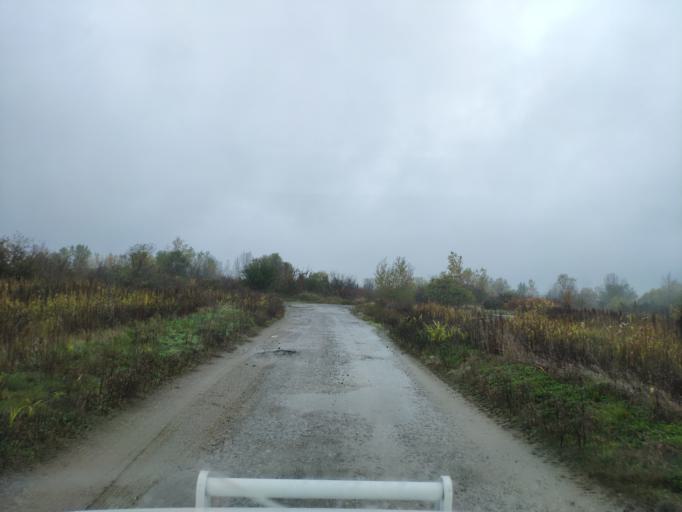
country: SK
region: Kosicky
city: Cierna nad Tisou
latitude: 48.4221
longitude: 21.9959
